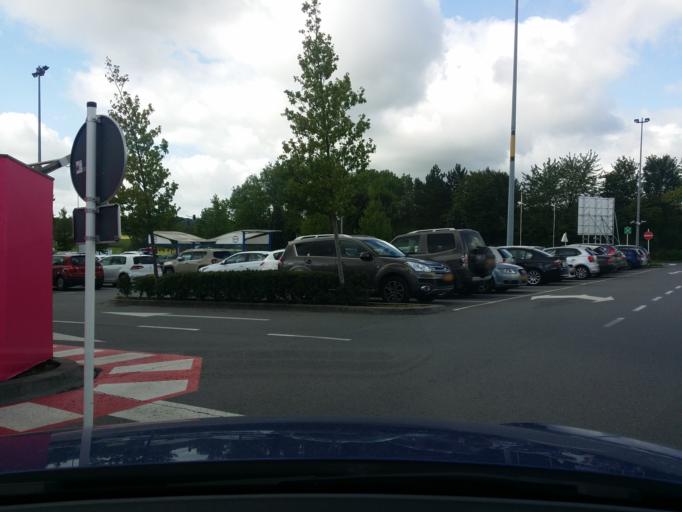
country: LU
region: Luxembourg
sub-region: Canton de Luxembourg
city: Bertrange
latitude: 49.6010
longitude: 6.0632
